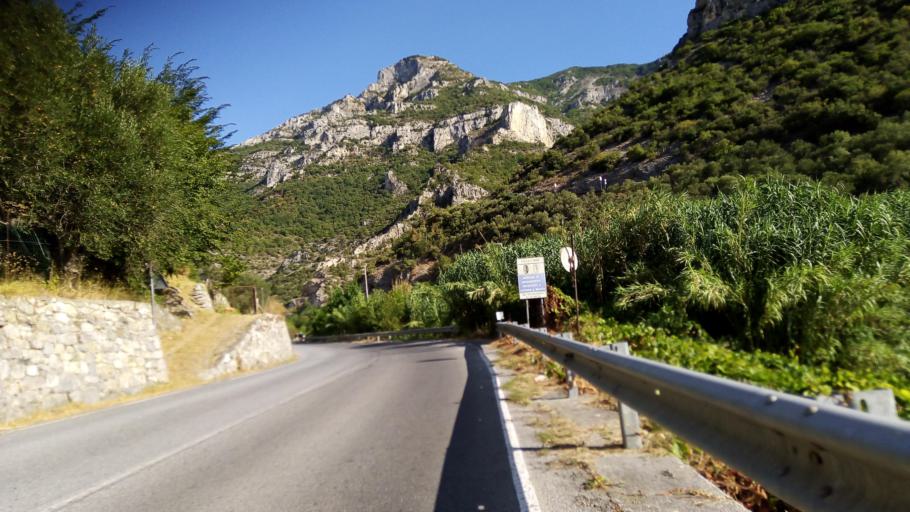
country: IT
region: Liguria
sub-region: Provincia di Savona
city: Toirano
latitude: 44.1323
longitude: 8.2014
